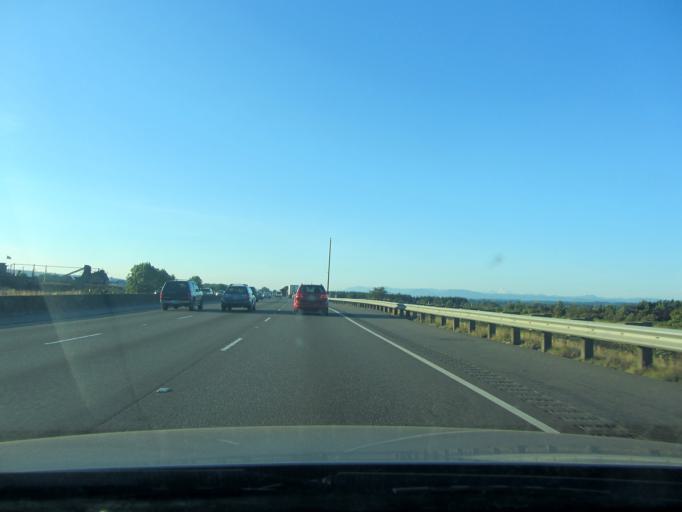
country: US
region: Washington
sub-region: Snohomish County
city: Marysville
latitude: 48.0184
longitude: -122.1749
